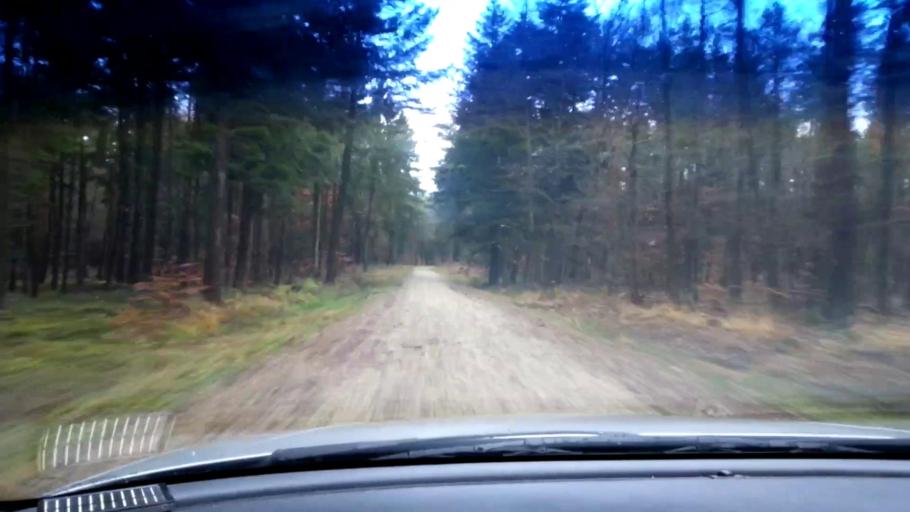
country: DE
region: Bavaria
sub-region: Upper Franconia
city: Kemmern
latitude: 49.9565
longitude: 10.8957
